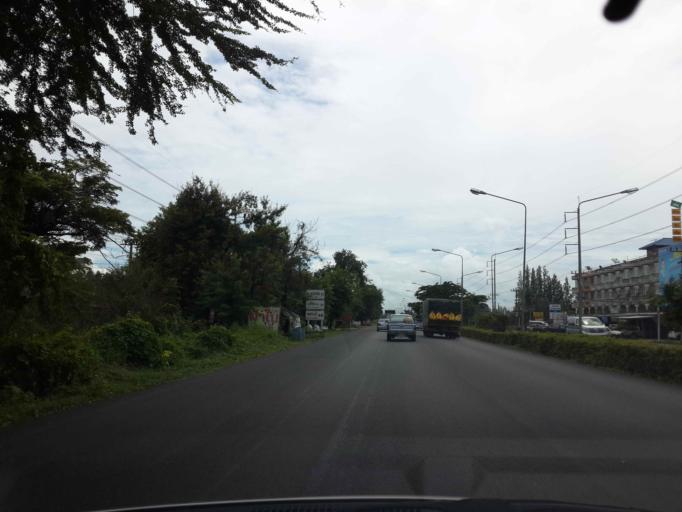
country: TH
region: Ratchaburi
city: Ratchaburi
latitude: 13.4540
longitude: 99.8005
